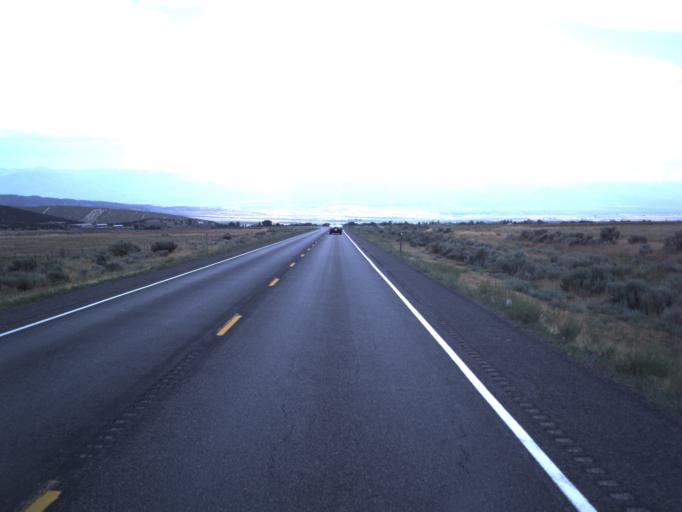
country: US
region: Utah
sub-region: Sanpete County
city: Fountain Green
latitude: 39.6541
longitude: -111.6503
